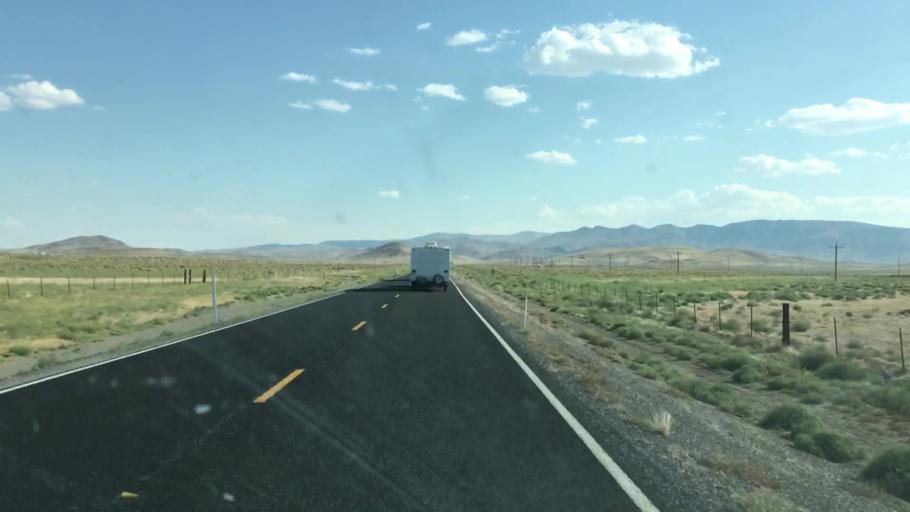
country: US
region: Nevada
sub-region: Lyon County
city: Fernley
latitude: 39.6620
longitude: -119.3316
